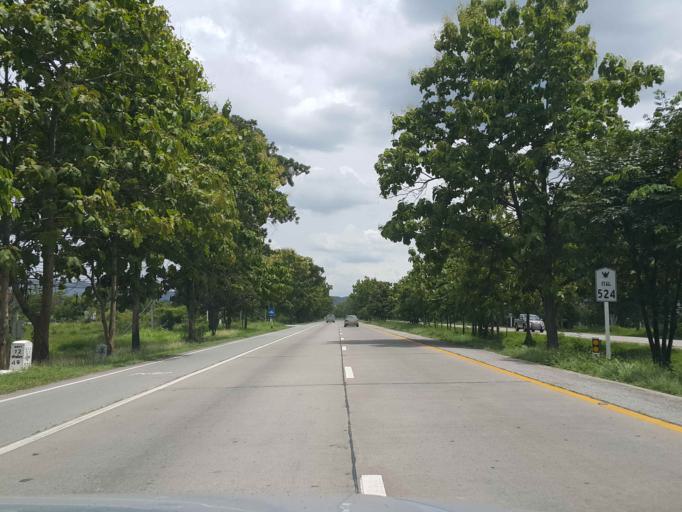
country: TH
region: Lamphun
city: Lamphun
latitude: 18.5313
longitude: 99.0785
